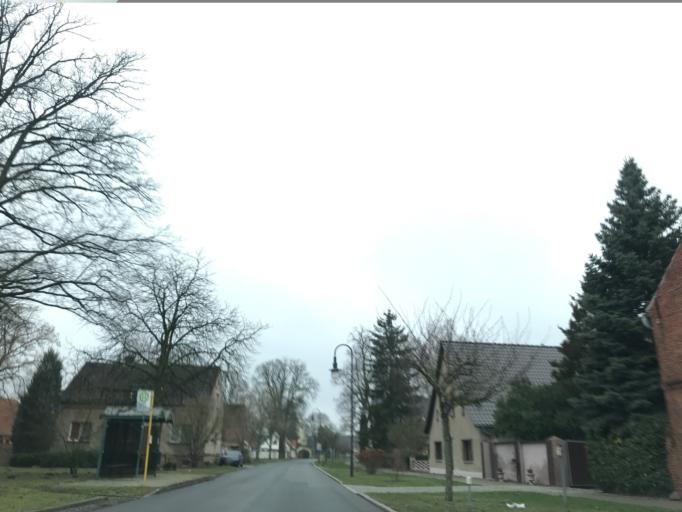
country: DE
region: Brandenburg
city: Brieselang
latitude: 52.6750
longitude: 12.9705
